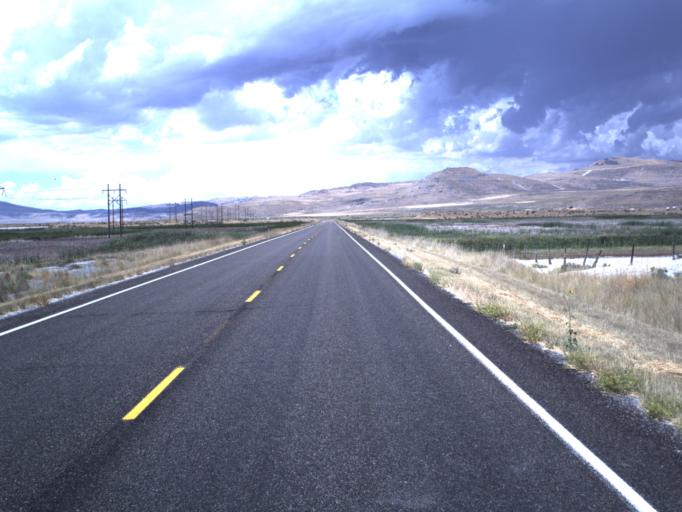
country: US
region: Utah
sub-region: Box Elder County
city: Tremonton
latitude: 41.6051
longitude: -112.3180
